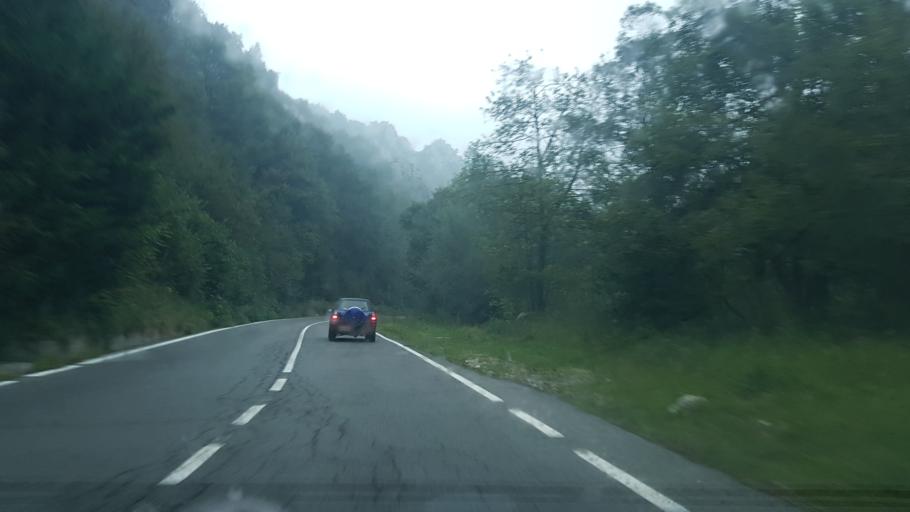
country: IT
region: Piedmont
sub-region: Provincia di Cuneo
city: Frabosa Soprana
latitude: 44.2641
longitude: 7.7660
